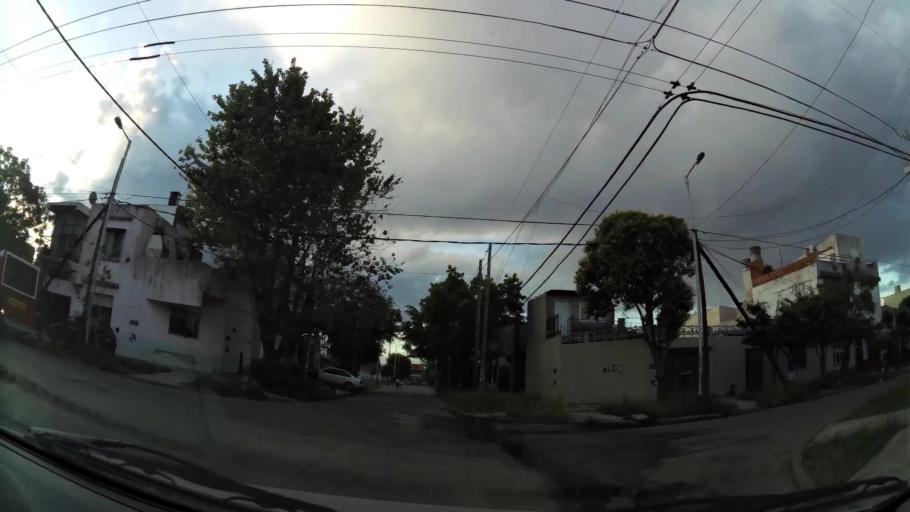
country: AR
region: Buenos Aires
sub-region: Partido de Avellaneda
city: Avellaneda
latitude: -34.6875
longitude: -58.3258
